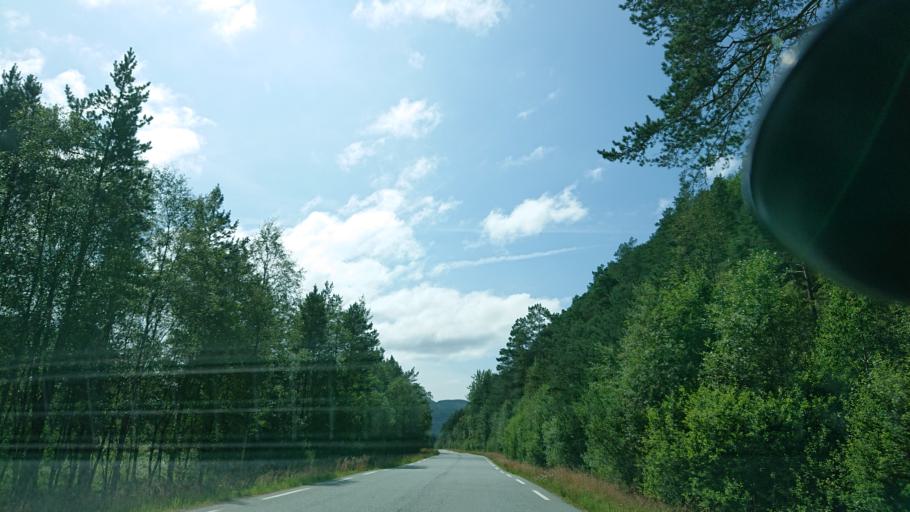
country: NO
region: Rogaland
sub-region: Hjelmeland
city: Hjelmelandsvagen
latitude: 59.2340
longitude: 6.2450
